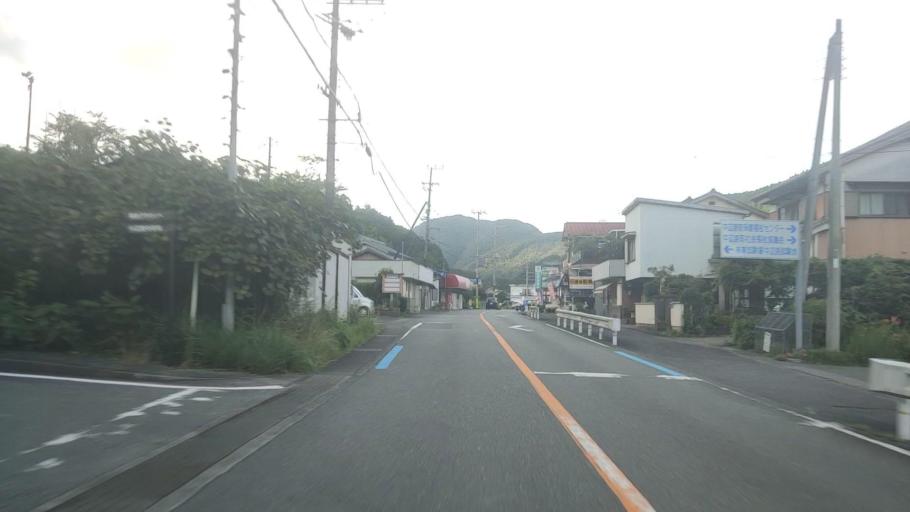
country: JP
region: Wakayama
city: Tanabe
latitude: 33.7915
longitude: 135.5164
